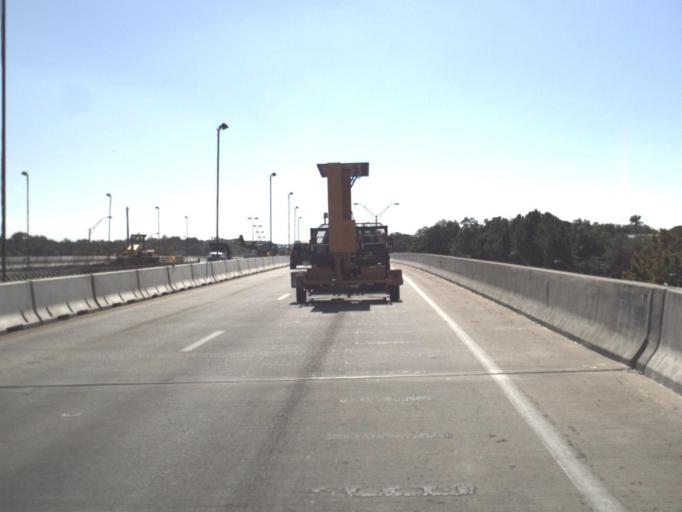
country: US
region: Florida
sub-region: Hillsborough County
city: Town 'n' Country
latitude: 27.9967
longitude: -82.5461
